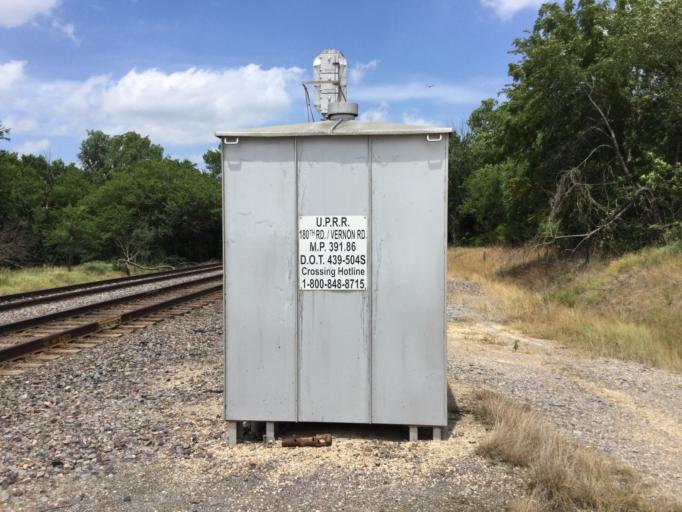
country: US
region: Kansas
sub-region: Woodson County
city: Yates Center
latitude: 37.9808
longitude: -95.6594
